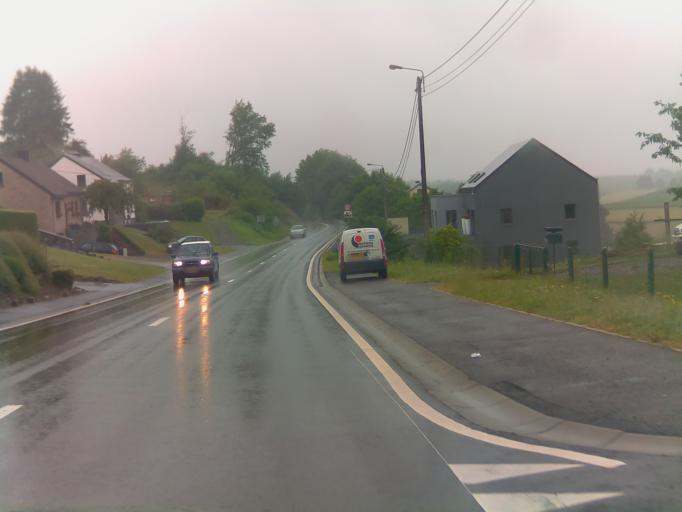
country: BE
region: Wallonia
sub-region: Province du Luxembourg
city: Neufchateau
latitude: 49.8426
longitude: 5.4253
